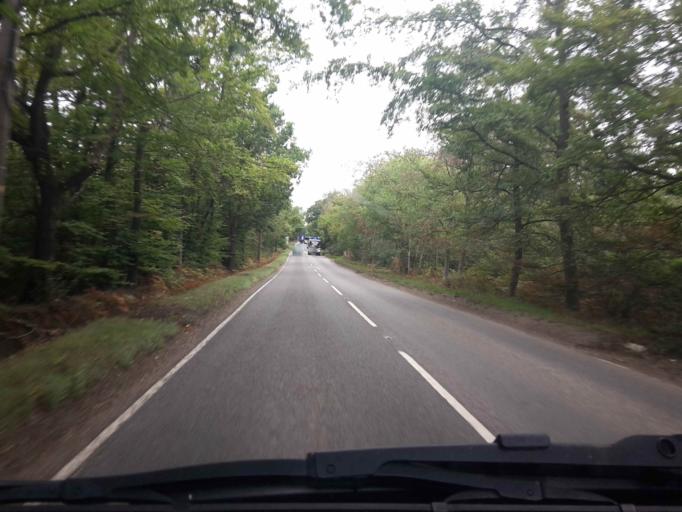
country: GB
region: England
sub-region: Hampshire
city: Eversley
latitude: 51.3225
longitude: -0.8696
